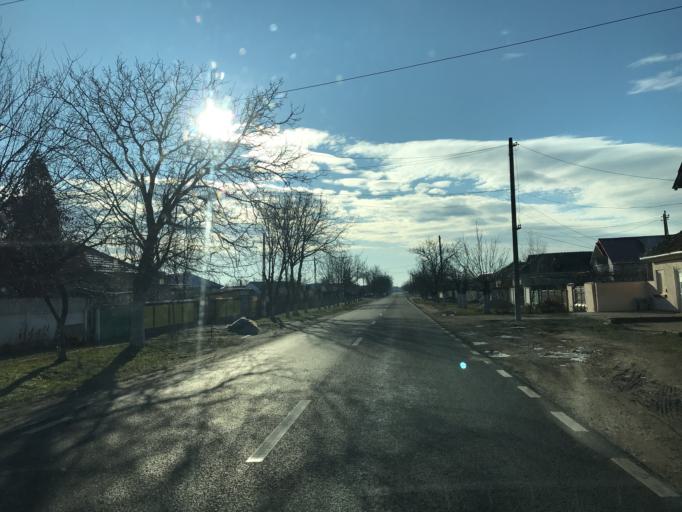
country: RO
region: Olt
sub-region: Comuna Piatra Olt
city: Piatra Olt
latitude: 44.3864
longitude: 24.2822
